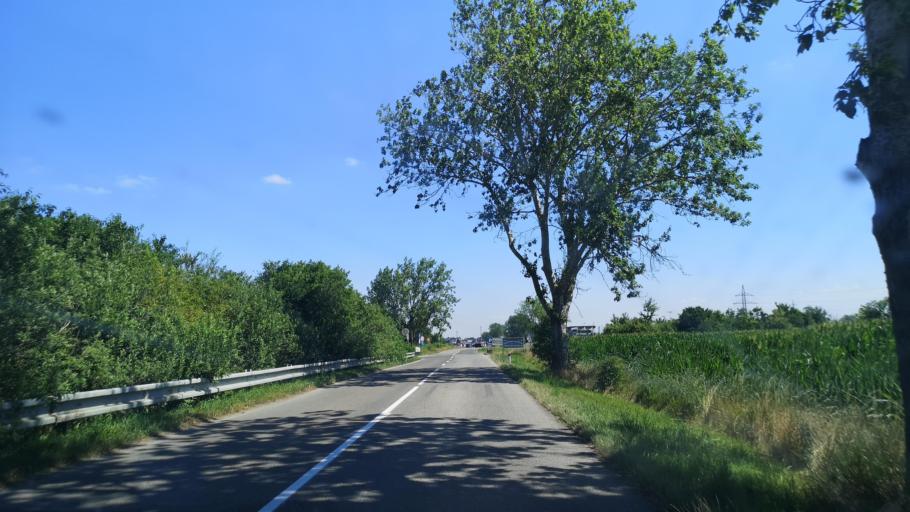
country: SK
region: Trnavsky
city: Dunajska Streda
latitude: 48.0460
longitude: 17.5638
